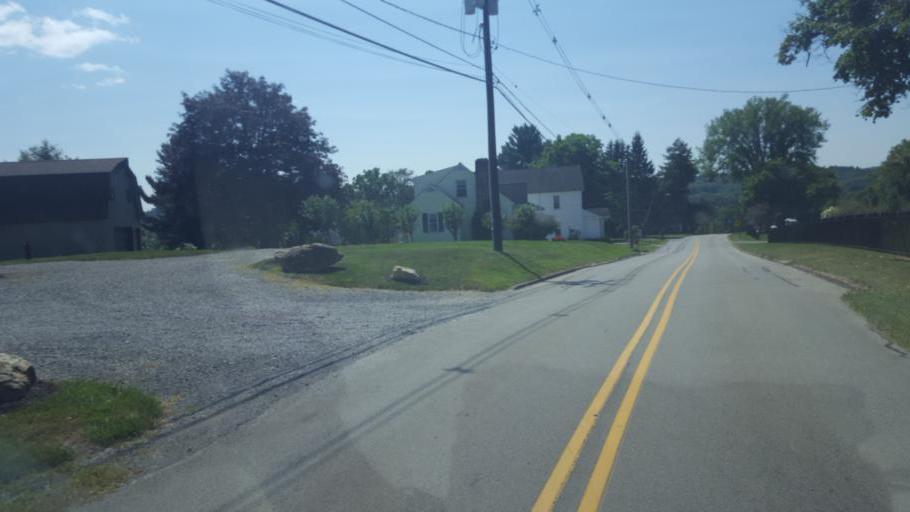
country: US
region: Pennsylvania
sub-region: Clarion County
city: Knox
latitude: 41.1837
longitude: -79.7111
